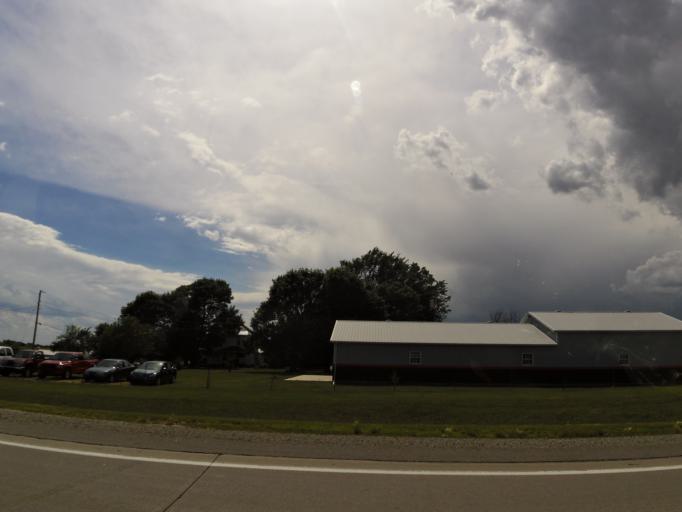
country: US
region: Iowa
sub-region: Henry County
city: Winfield
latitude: 41.2146
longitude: -91.5293
